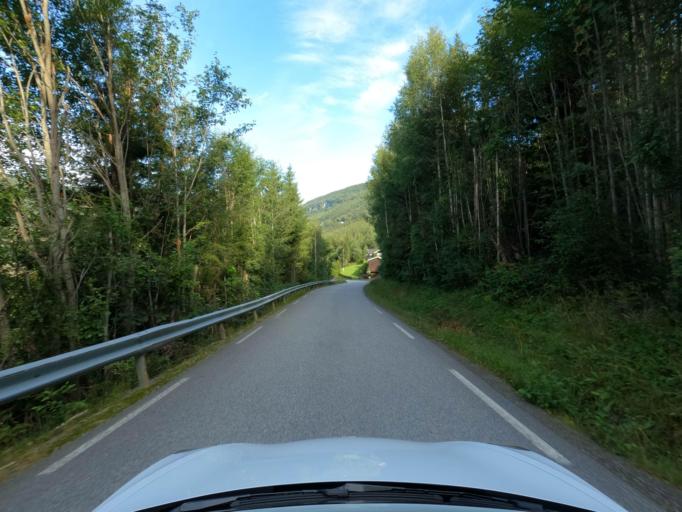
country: NO
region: Buskerud
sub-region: Nore og Uvdal
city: Rodberg
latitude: 60.0468
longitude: 8.8246
